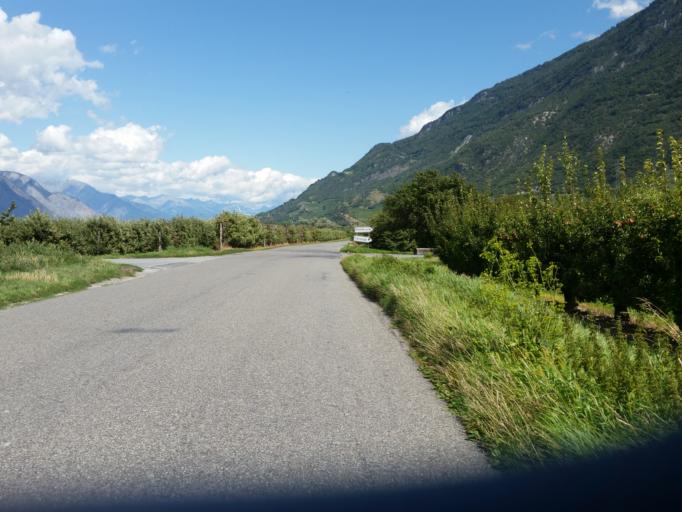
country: CH
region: Valais
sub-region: Martigny District
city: Charrat-les-Chenes
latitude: 46.1146
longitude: 7.1135
